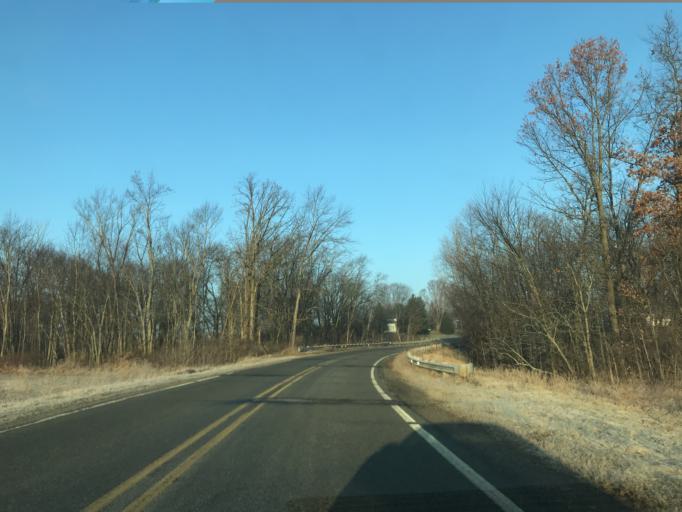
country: US
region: Michigan
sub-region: Ingham County
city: Leslie
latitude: 42.4030
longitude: -84.4845
